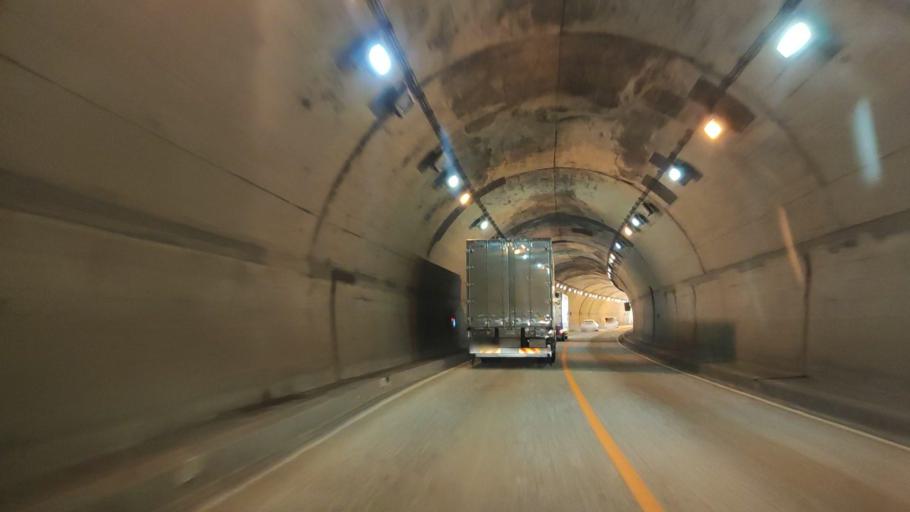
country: JP
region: Aomori
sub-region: Misawa Shi
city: Inuotose
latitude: 40.7823
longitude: 141.0597
